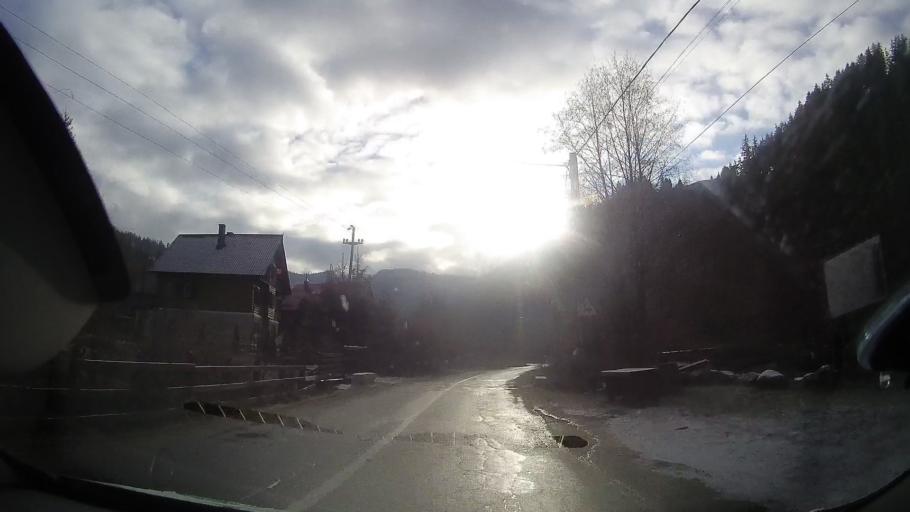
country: RO
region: Alba
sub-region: Comuna Albac
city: Albac
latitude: 46.4633
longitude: 22.9696
